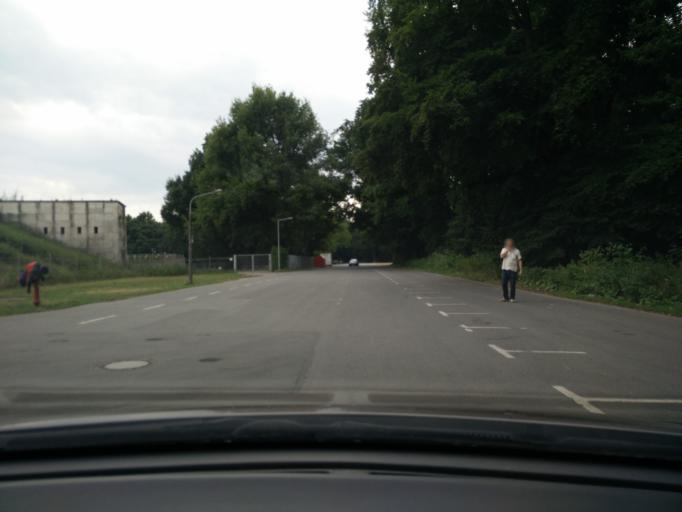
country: DE
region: Bavaria
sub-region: Regierungsbezirk Mittelfranken
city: Nuernberg
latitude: 49.4307
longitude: 11.1208
